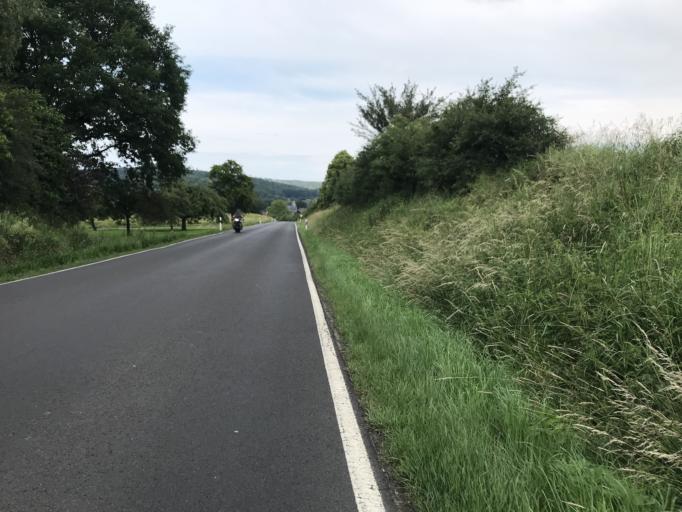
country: DE
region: Hesse
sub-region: Regierungsbezirk Giessen
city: Laubach
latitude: 50.5367
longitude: 8.9821
